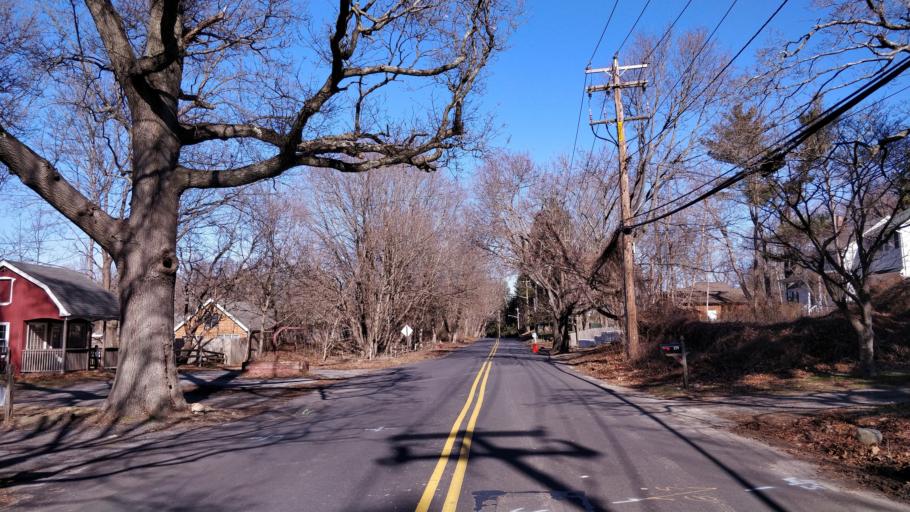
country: US
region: New York
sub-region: Suffolk County
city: Head of the Harbor
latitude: 40.8938
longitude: -73.1464
